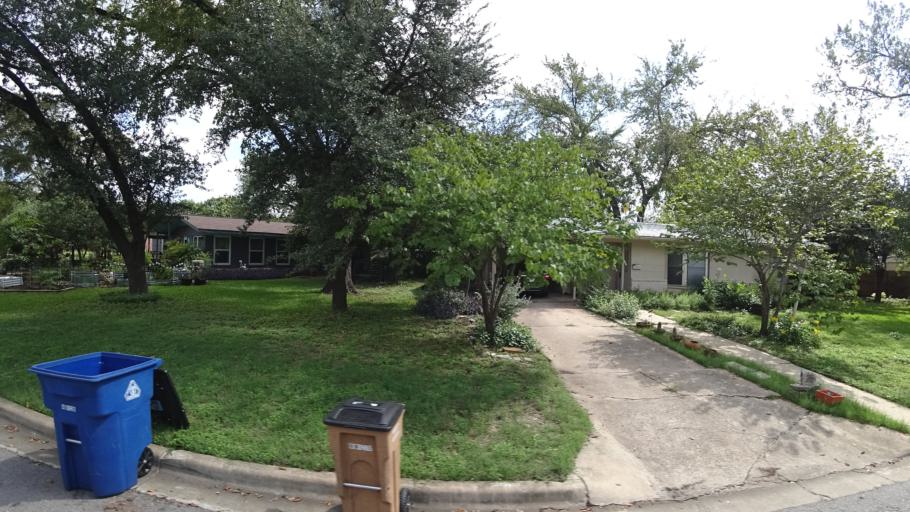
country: US
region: Texas
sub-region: Travis County
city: Austin
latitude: 30.3500
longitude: -97.7218
